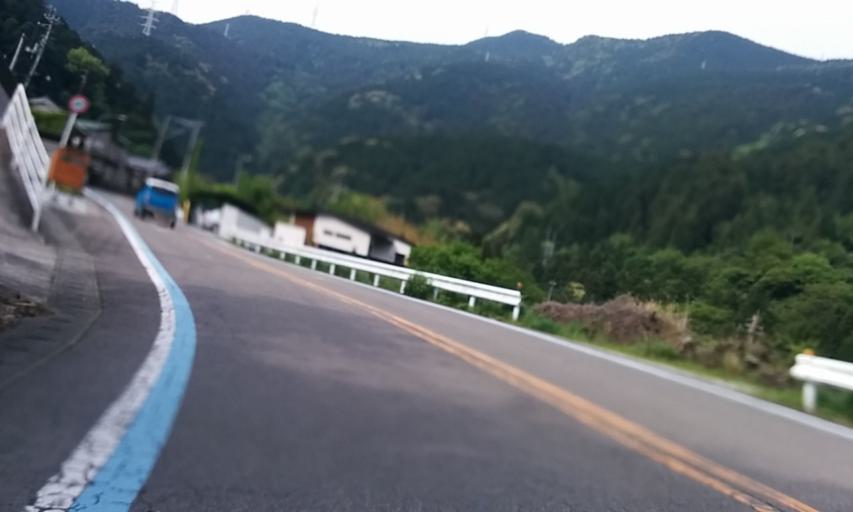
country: JP
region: Ehime
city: Niihama
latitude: 33.9100
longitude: 133.3088
